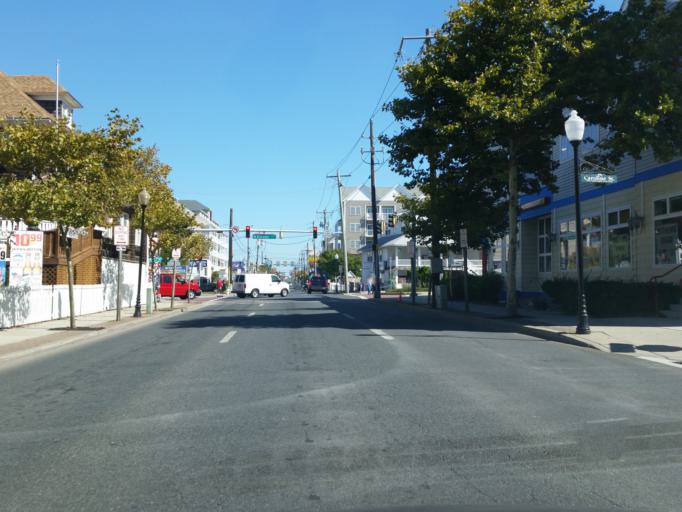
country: US
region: Maryland
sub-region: Worcester County
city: Ocean City
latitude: 38.3311
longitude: -75.0864
